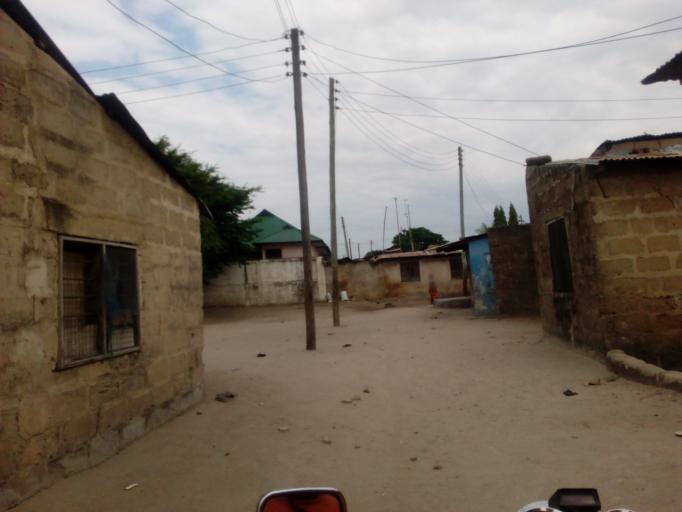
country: TZ
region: Dar es Salaam
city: Dar es Salaam
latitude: -6.8560
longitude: 39.2506
